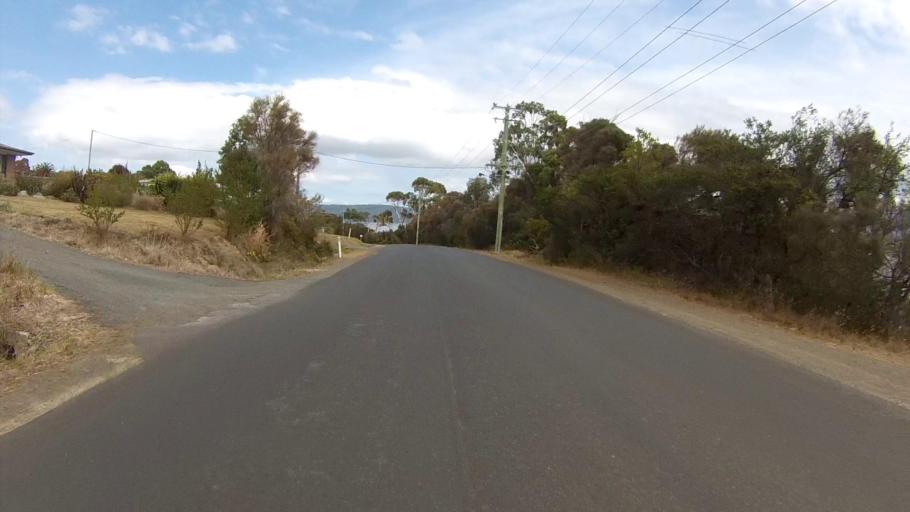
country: AU
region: Tasmania
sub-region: Kingborough
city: Margate
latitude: -43.0244
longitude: 147.2909
